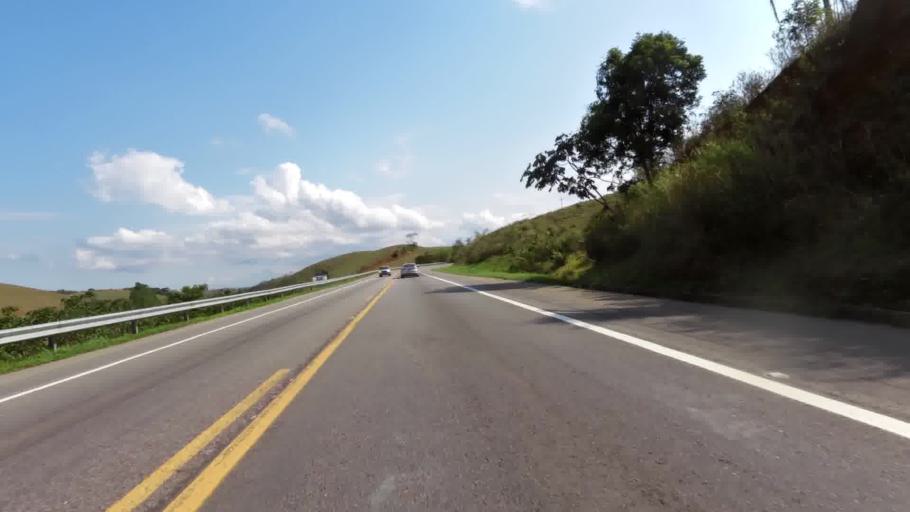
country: BR
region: Rio de Janeiro
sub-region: Macae
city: Macae
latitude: -22.2476
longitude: -41.8105
